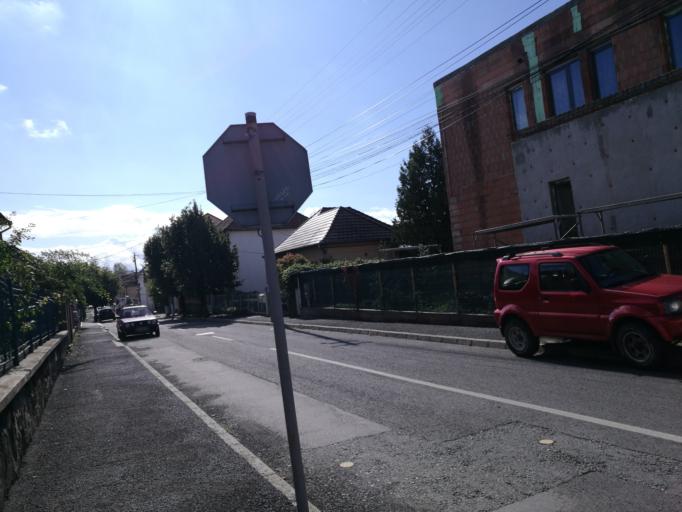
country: RO
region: Sibiu
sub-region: Municipiul Sibiu
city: Sibiu
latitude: 45.7842
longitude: 24.1577
